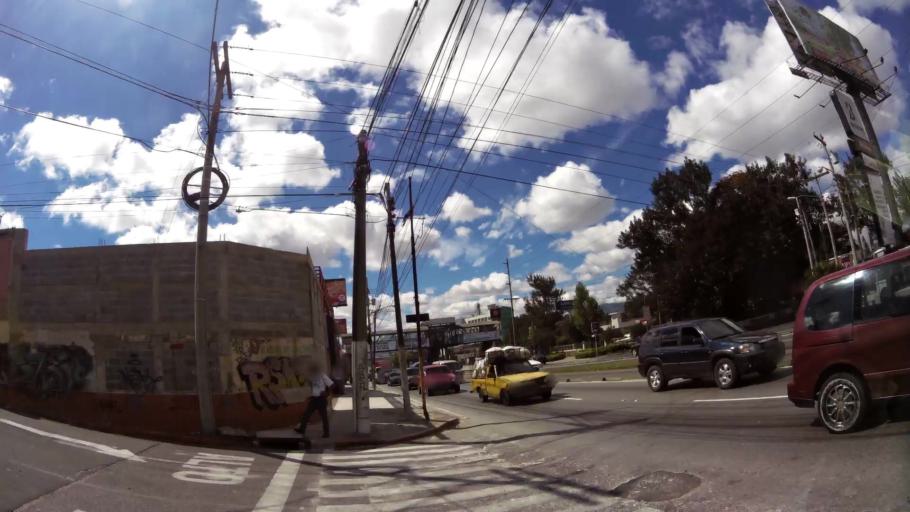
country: GT
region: Guatemala
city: Guatemala City
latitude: 14.6028
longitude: -90.5473
